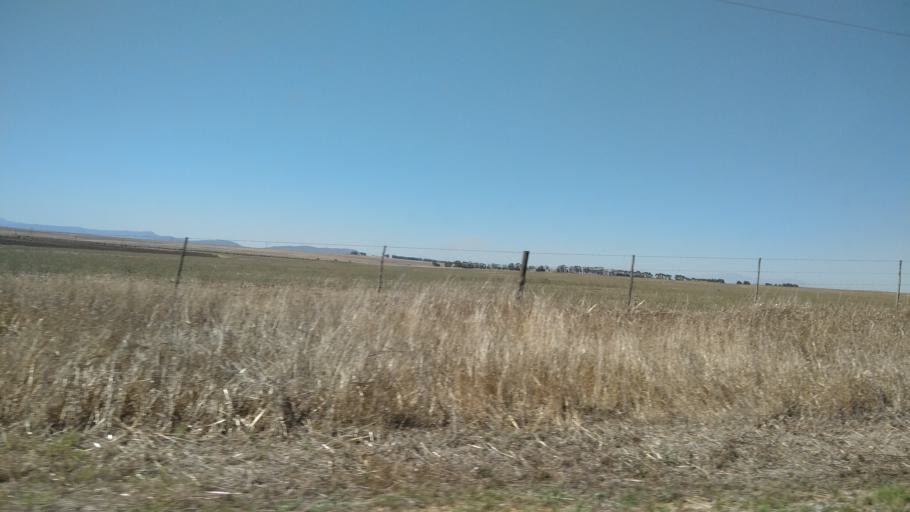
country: ZA
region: Western Cape
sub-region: West Coast District Municipality
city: Moorreesburg
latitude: -33.1732
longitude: 18.4843
